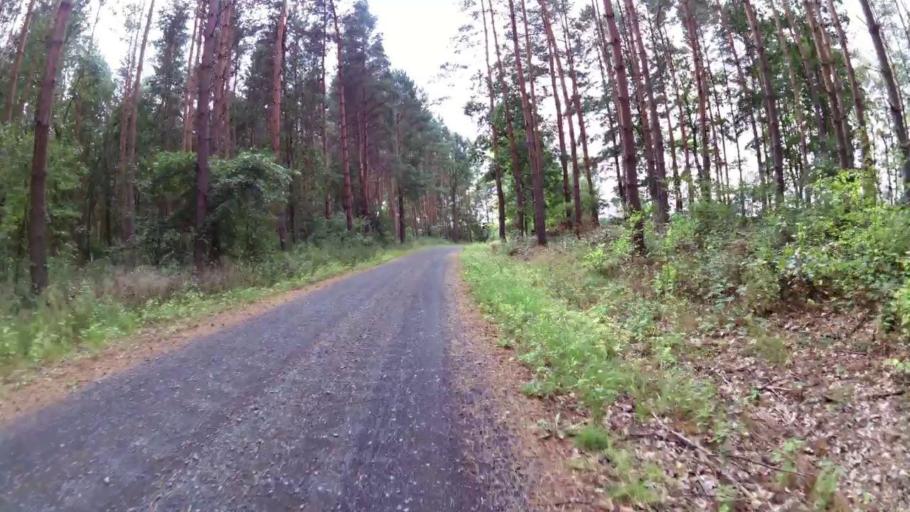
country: PL
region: West Pomeranian Voivodeship
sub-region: Powiat mysliborski
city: Debno
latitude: 52.7662
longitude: 14.7138
